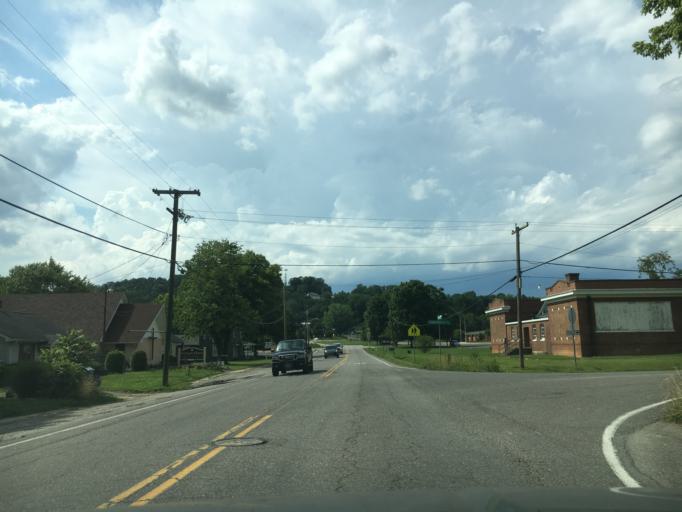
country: US
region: Virginia
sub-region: Roanoke County
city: Cave Spring
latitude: 37.2015
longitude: -79.9990
